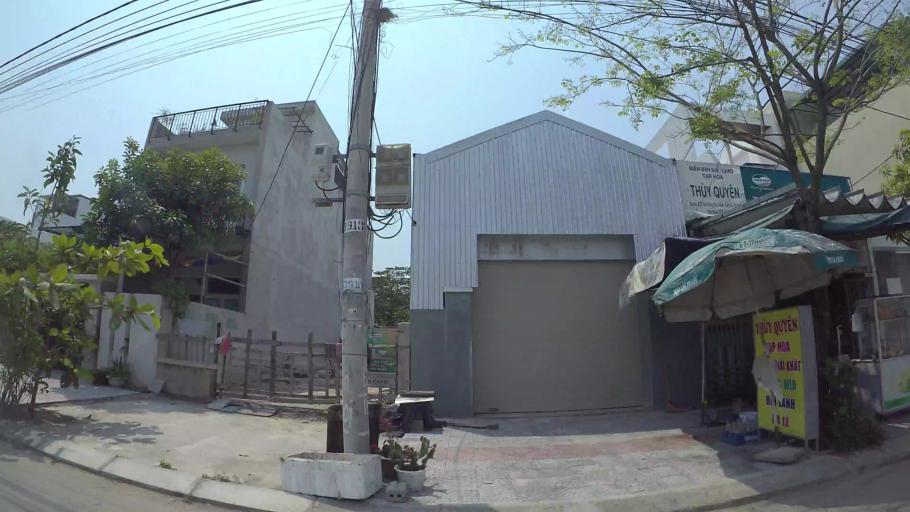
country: VN
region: Da Nang
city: Cam Le
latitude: 16.0123
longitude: 108.2203
